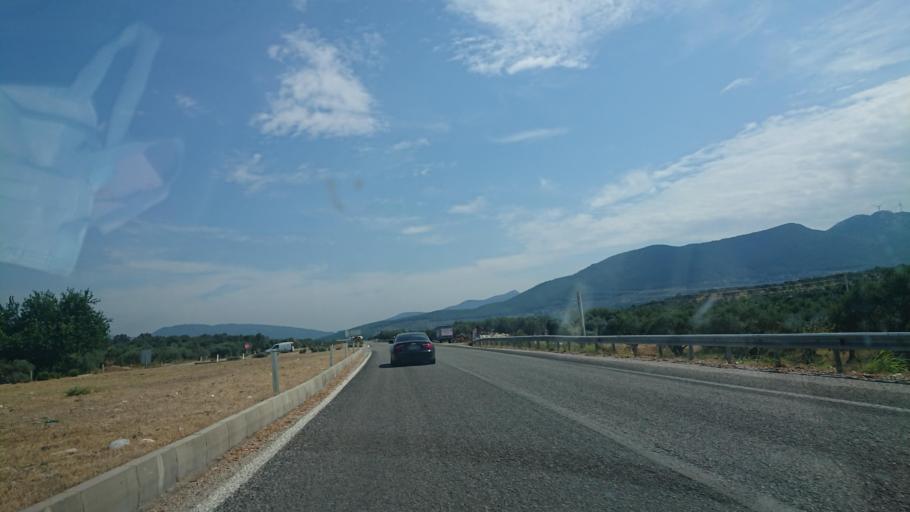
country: TR
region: Izmir
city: Dagkizilca
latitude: 38.2800
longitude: 27.4002
